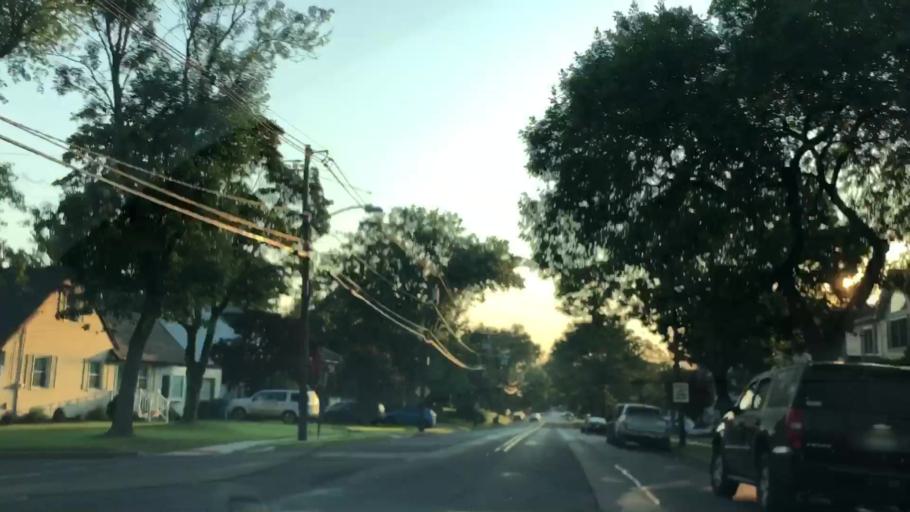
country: US
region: New Jersey
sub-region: Union County
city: Winfield
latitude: 40.6261
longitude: -74.2914
